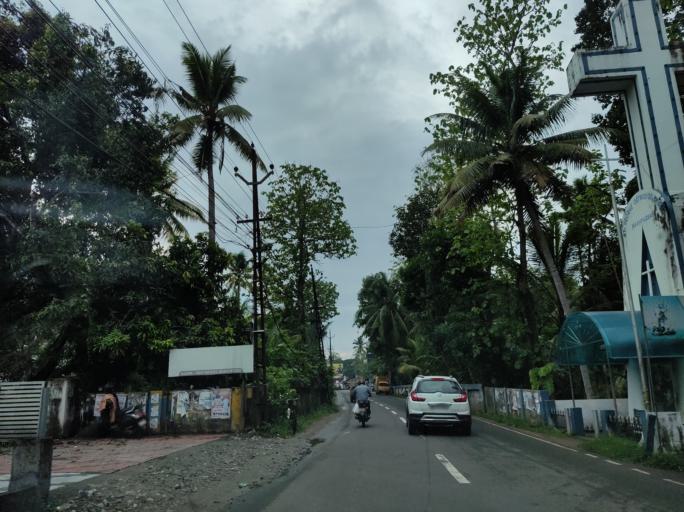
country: IN
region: Kerala
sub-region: Alappuzha
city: Mavelikara
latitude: 9.2519
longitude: 76.5067
